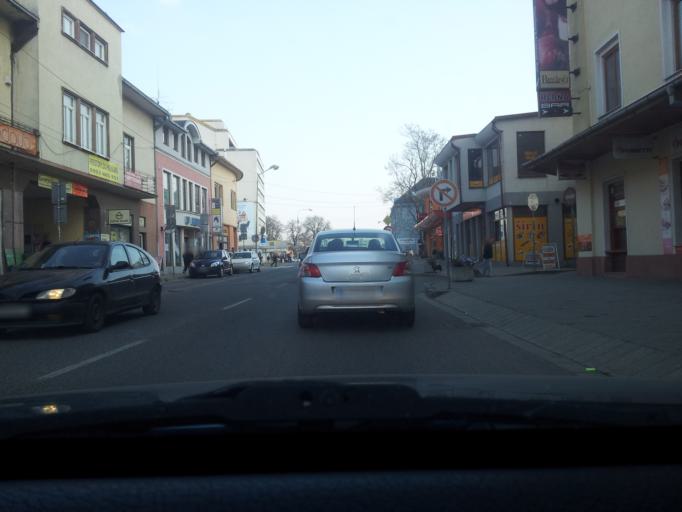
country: SK
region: Nitriansky
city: Levice
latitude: 48.2178
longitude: 18.6037
